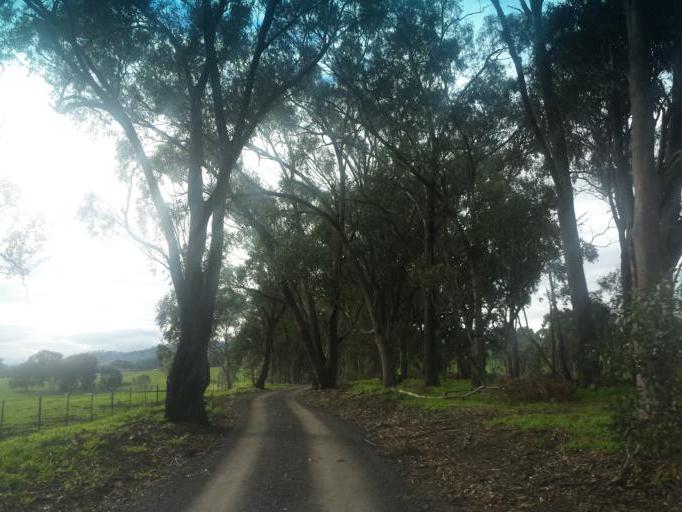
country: AU
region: Victoria
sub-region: Murrindindi
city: Kinglake West
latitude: -37.0307
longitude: 145.2502
